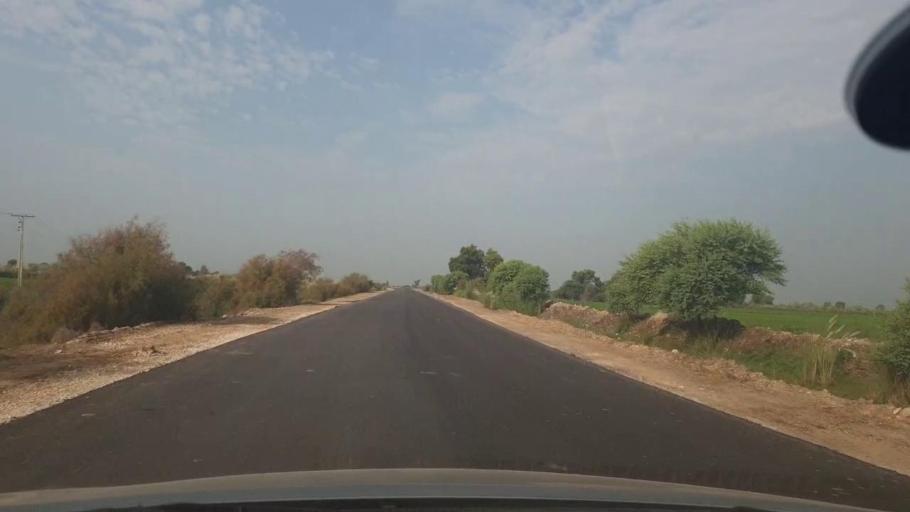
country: PK
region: Sindh
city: Jacobabad
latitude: 28.1296
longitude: 68.3317
